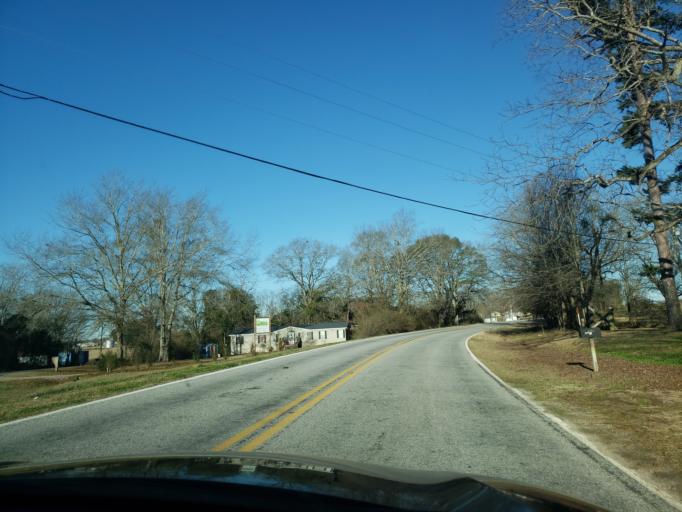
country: US
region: Alabama
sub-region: Elmore County
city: Tallassee
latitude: 32.5814
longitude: -85.7888
